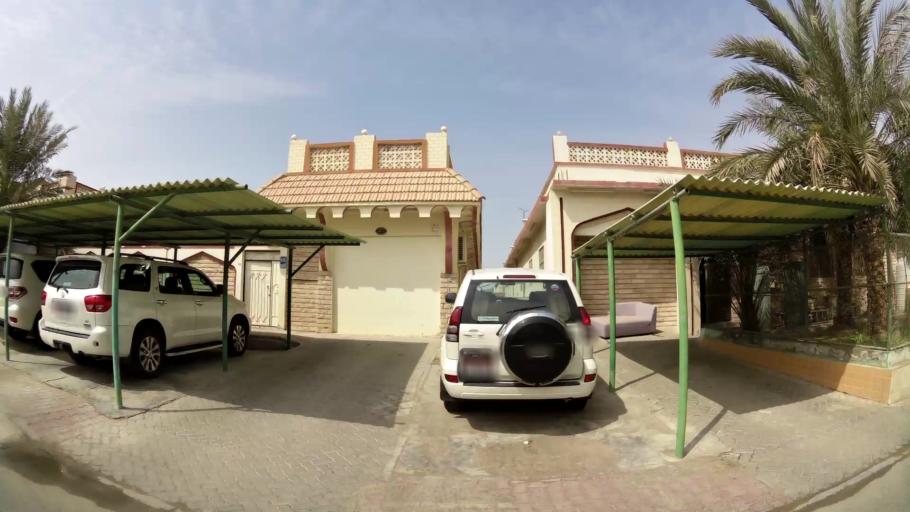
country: AE
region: Abu Dhabi
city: Abu Dhabi
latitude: 24.5463
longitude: 54.6825
